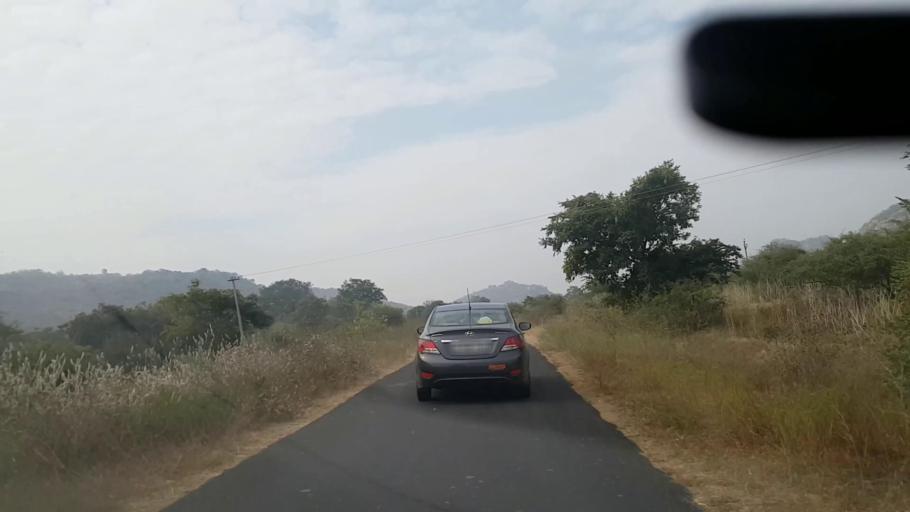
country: IN
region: Telangana
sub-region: Rangareddi
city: Ghatkesar
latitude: 17.1761
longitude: 78.8215
